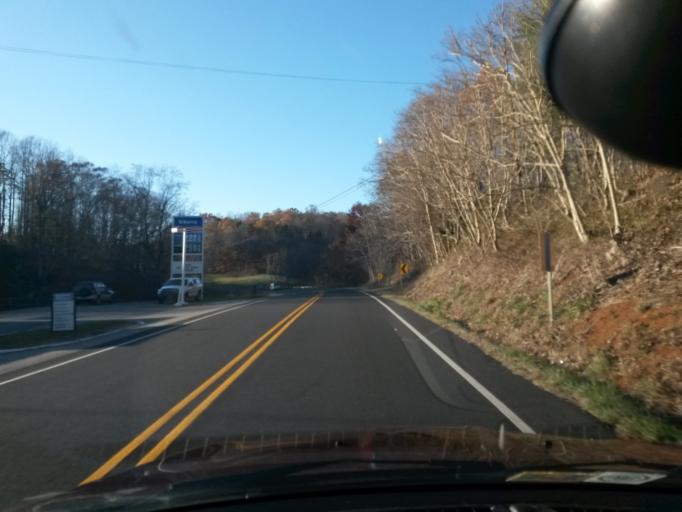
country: US
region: Virginia
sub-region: Amherst County
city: Amherst
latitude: 37.6653
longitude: -79.1634
